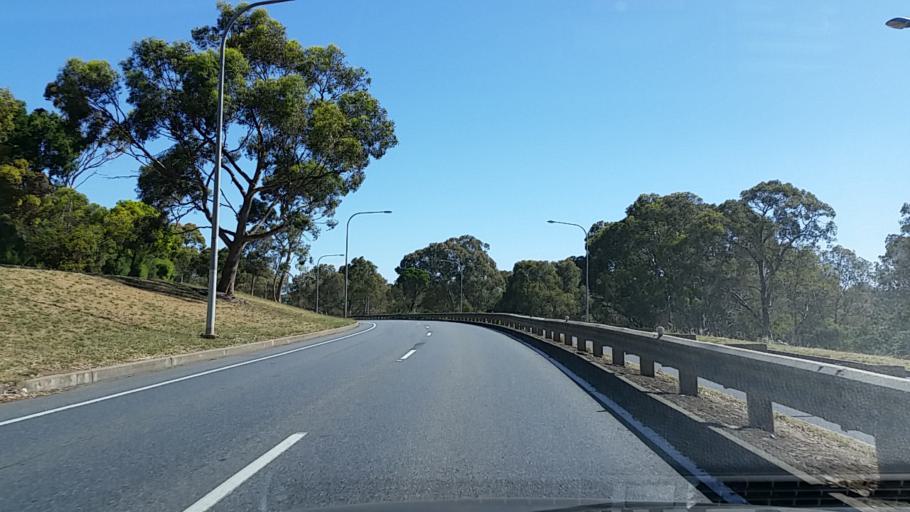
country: AU
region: South Australia
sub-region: Tea Tree Gully
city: Hope Valley
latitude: -34.8134
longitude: 138.6943
